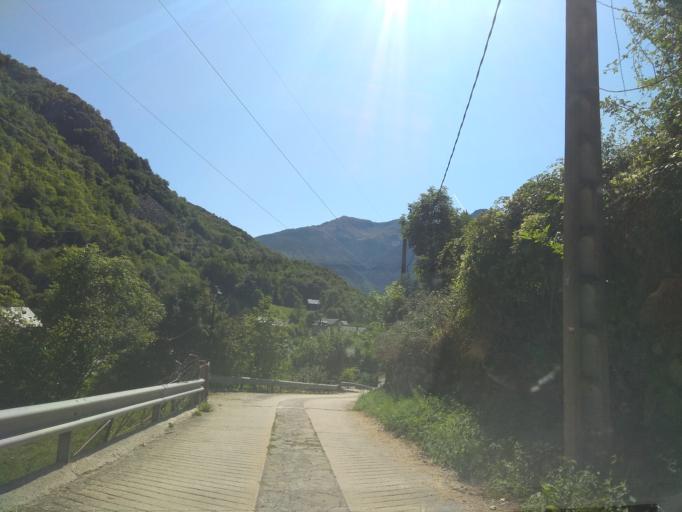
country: ES
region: Catalonia
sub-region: Provincia de Lleida
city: Les
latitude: 42.7517
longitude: 0.6976
